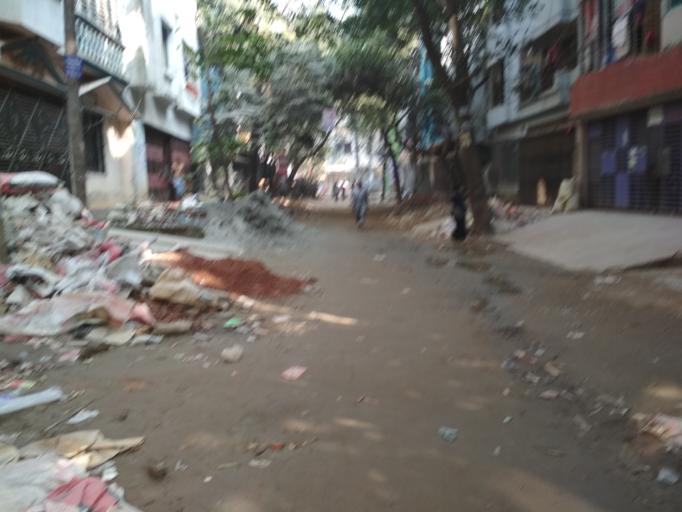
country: BD
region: Dhaka
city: Azimpur
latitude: 23.8088
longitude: 90.3714
